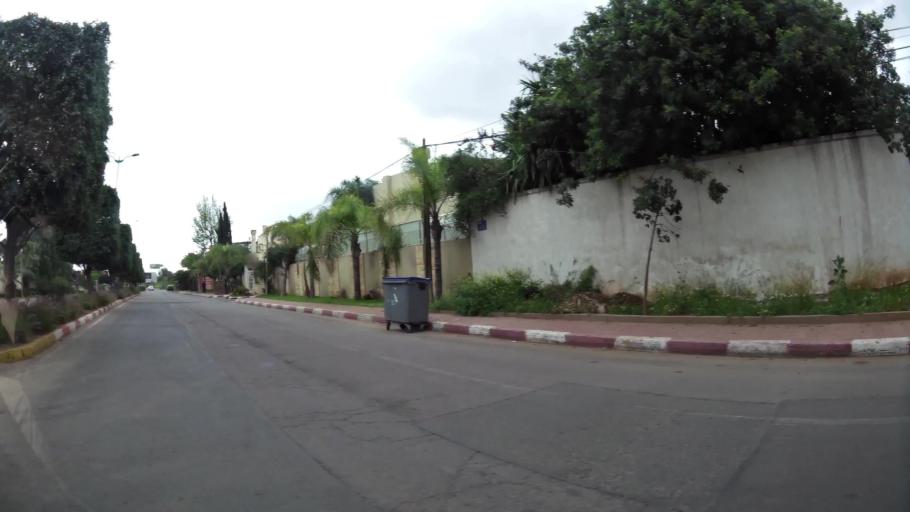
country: MA
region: Grand Casablanca
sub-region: Casablanca
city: Casablanca
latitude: 33.5235
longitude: -7.6326
